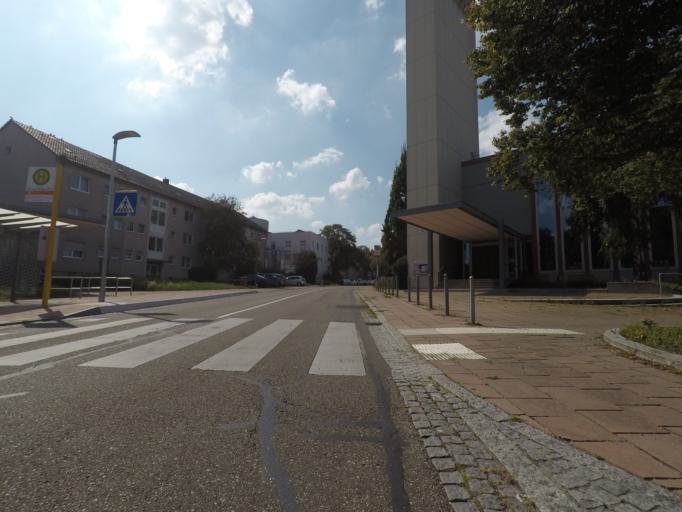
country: DE
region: Baden-Wuerttemberg
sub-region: Regierungsbezirk Stuttgart
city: Ostfildern
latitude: 48.7263
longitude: 9.2728
